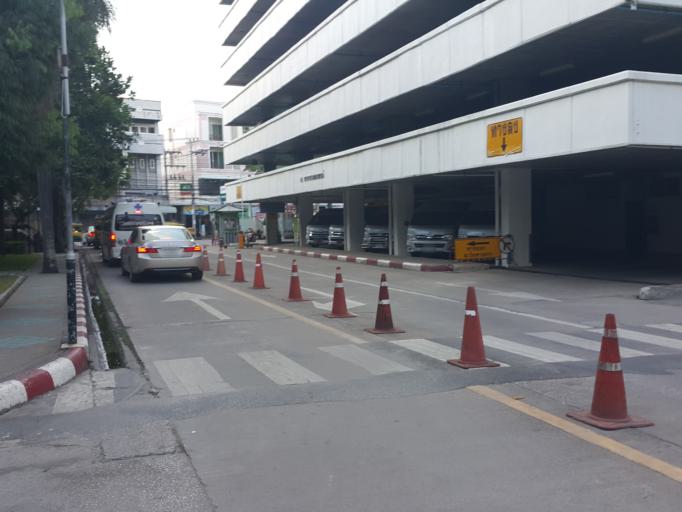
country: TH
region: Lampang
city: Lampang
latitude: 18.2868
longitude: 99.5057
